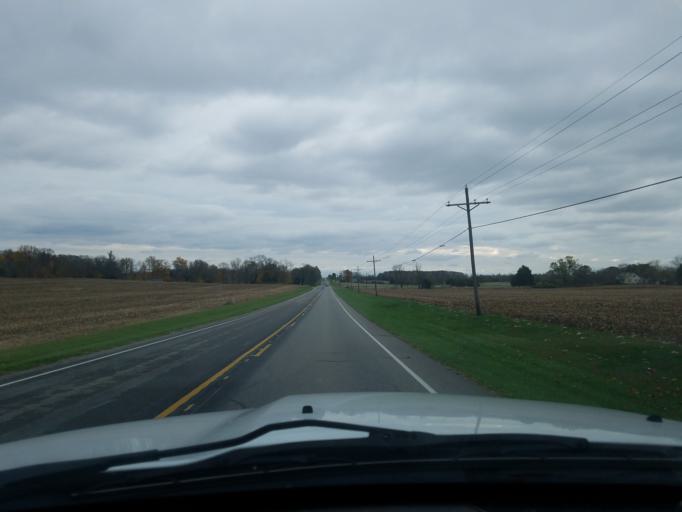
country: US
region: Indiana
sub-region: Bartholomew County
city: Hope
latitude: 39.2603
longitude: -85.7714
